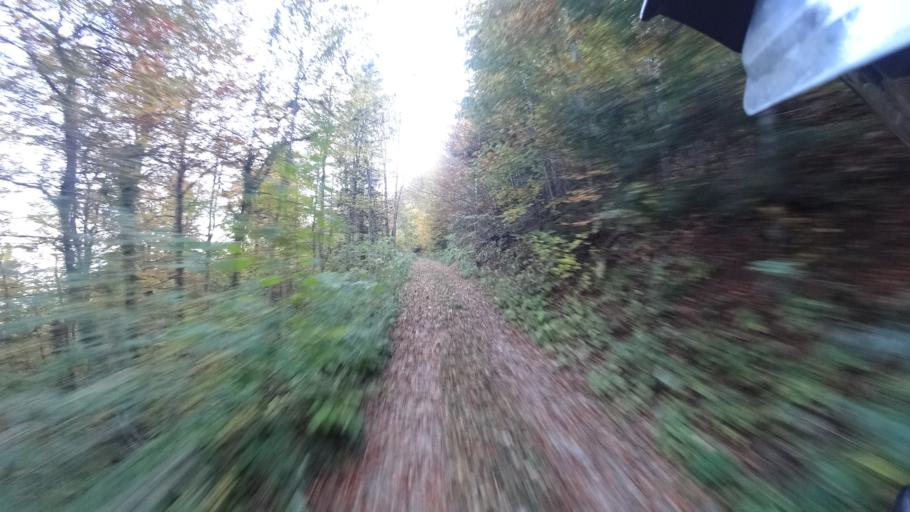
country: HR
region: Karlovacka
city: Plaski
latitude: 45.0138
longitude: 15.3851
